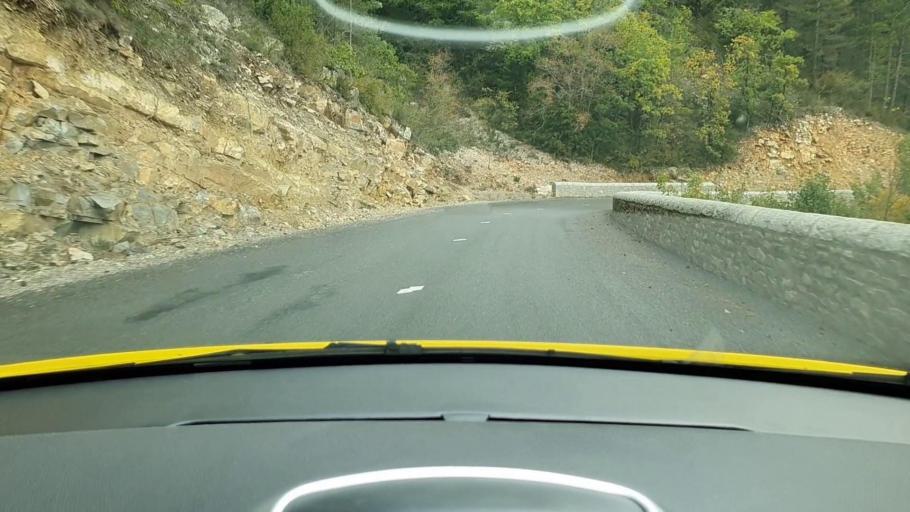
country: FR
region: Languedoc-Roussillon
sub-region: Departement de la Lozere
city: Meyrueis
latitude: 44.0802
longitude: 3.3746
